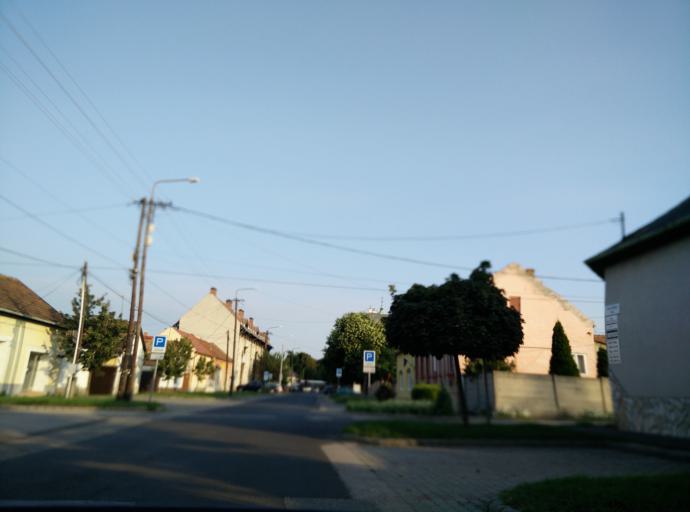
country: HU
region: Heves
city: Hatvan
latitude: 47.6651
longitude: 19.6864
